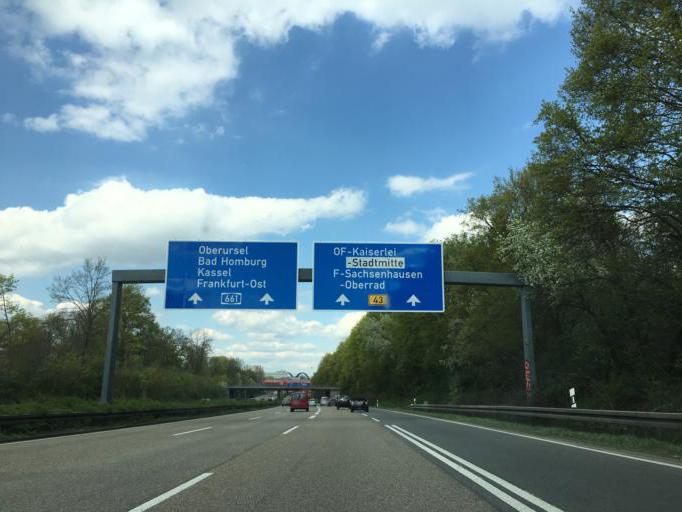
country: DE
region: Hesse
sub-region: Regierungsbezirk Darmstadt
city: Offenbach
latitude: 50.0984
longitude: 8.7407
